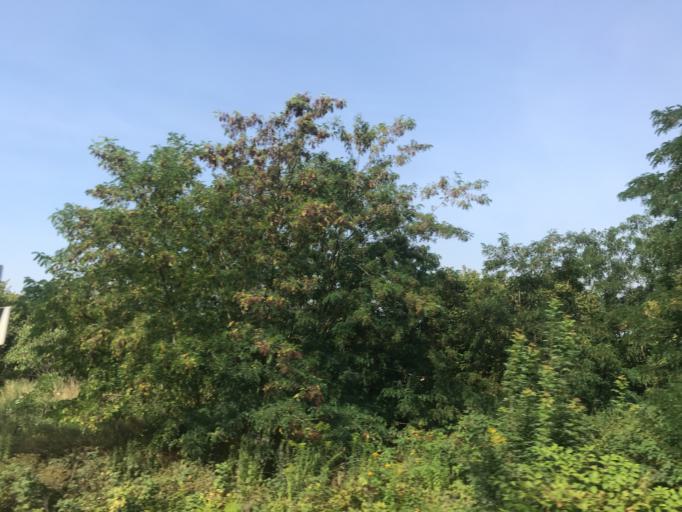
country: CZ
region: Central Bohemia
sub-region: Okres Praha-Vychod
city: Strancice
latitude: 49.9576
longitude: 14.6540
